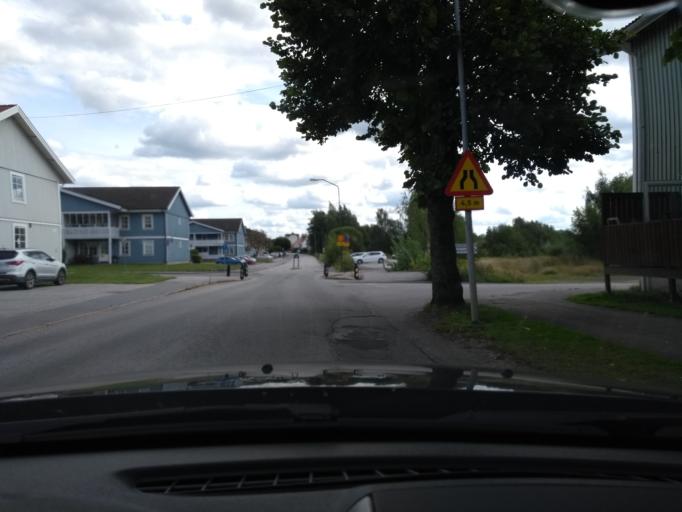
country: SE
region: Kalmar
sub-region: Vimmerby Kommun
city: Vimmerby
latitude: 57.6641
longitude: 15.8598
